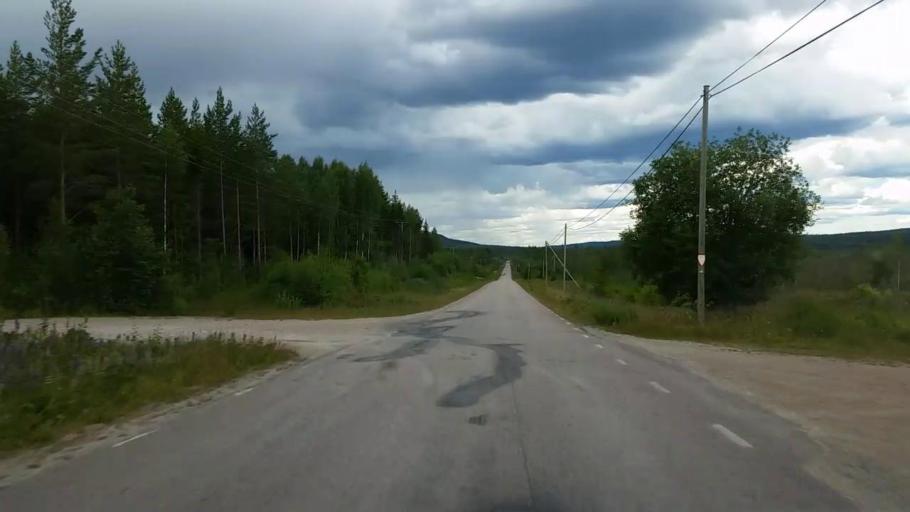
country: SE
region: Gaevleborg
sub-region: Ovanakers Kommun
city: Edsbyn
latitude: 61.4378
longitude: 15.8935
